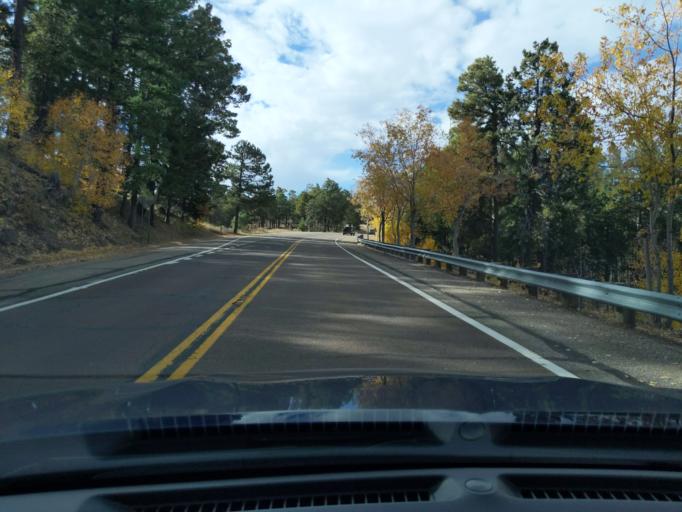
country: US
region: Arizona
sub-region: Pinal County
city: Oracle
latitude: 32.4325
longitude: -110.7495
